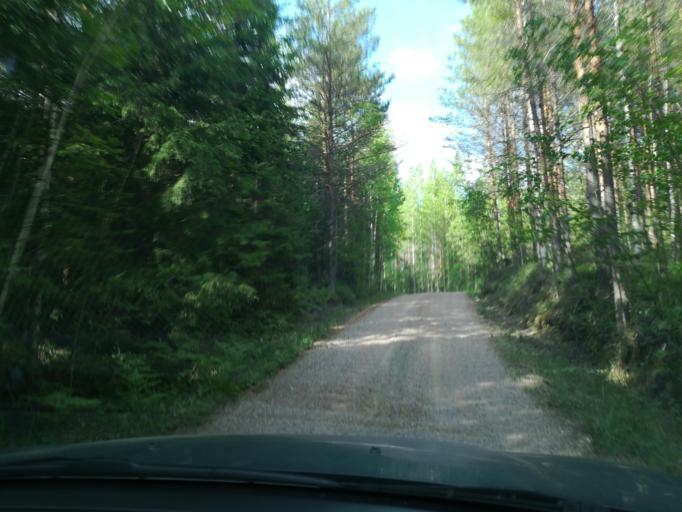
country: FI
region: Southern Savonia
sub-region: Savonlinna
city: Savonlinna
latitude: 61.6448
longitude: 28.7178
